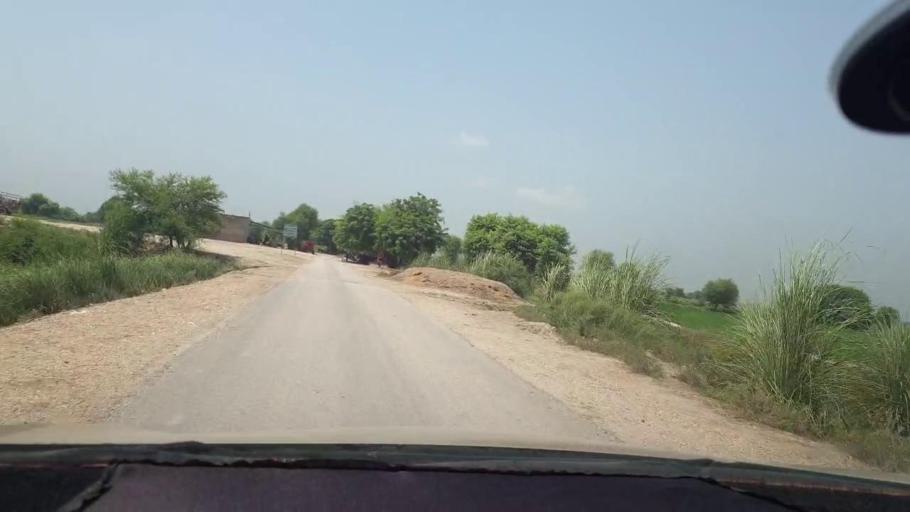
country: PK
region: Sindh
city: Kambar
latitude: 27.6631
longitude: 67.9367
